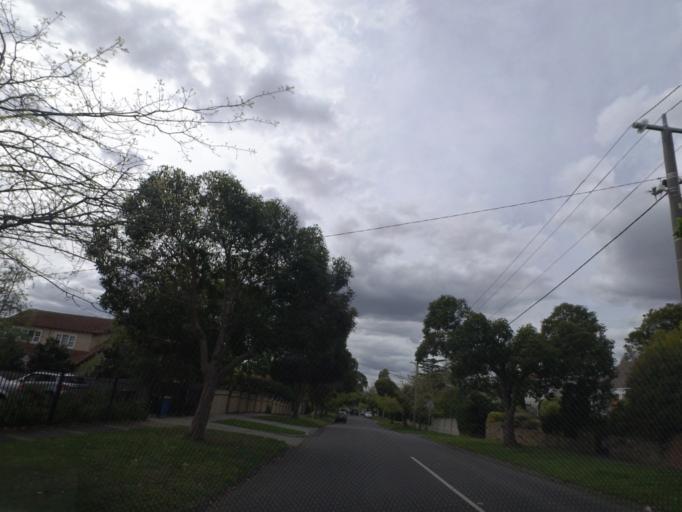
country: AU
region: Victoria
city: Mont Albert
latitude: -37.8099
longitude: 145.0958
